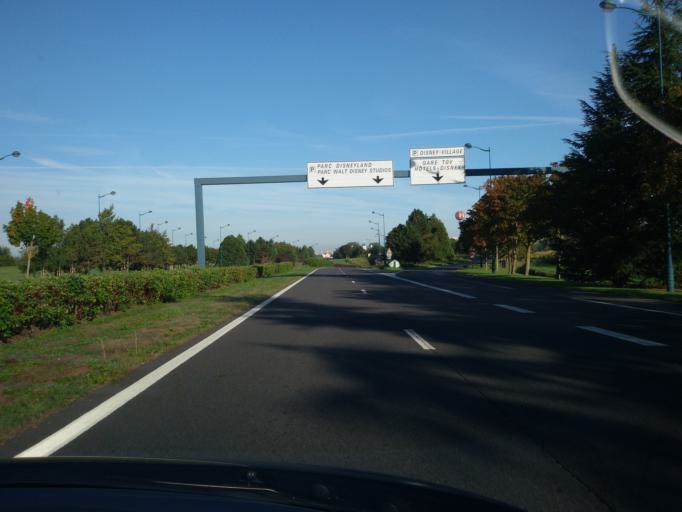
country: FR
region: Ile-de-France
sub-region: Departement de Seine-et-Marne
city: Serris
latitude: 48.8571
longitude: 2.7973
